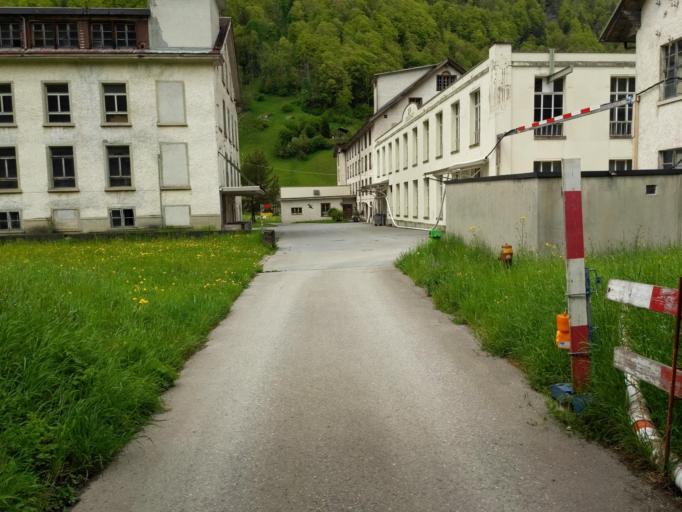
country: CH
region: Glarus
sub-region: Glarus
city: Luchsingen
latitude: 46.9509
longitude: 9.0290
